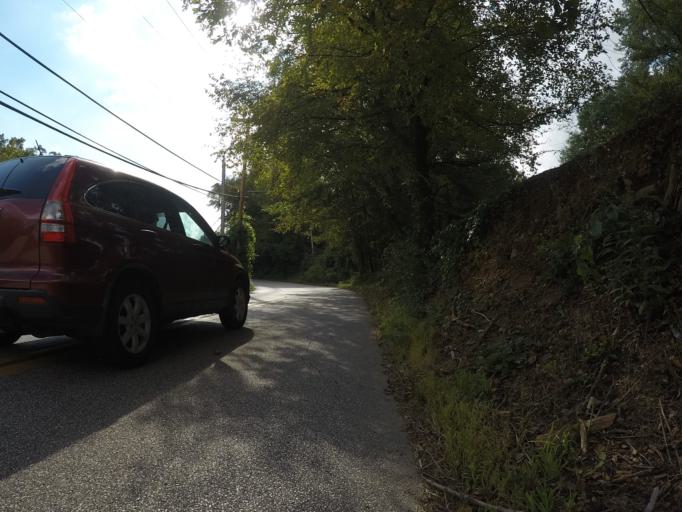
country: US
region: West Virginia
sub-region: Cabell County
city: Huntington
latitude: 38.4031
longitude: -82.4384
